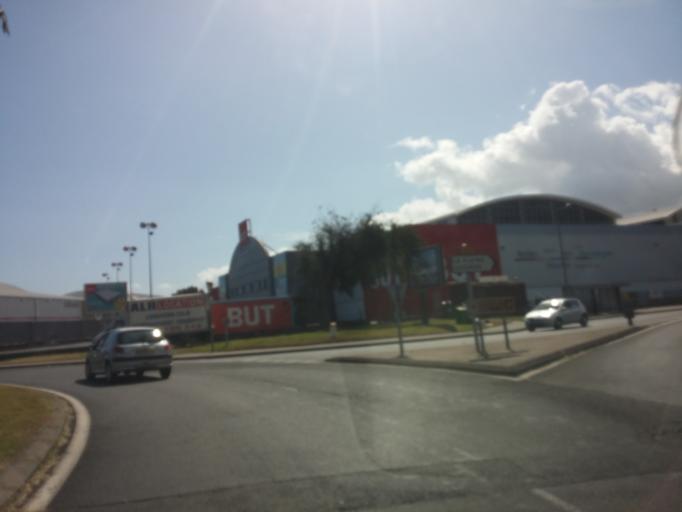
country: RE
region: Reunion
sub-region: Reunion
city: Saint-Paul
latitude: -20.9882
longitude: 55.2922
